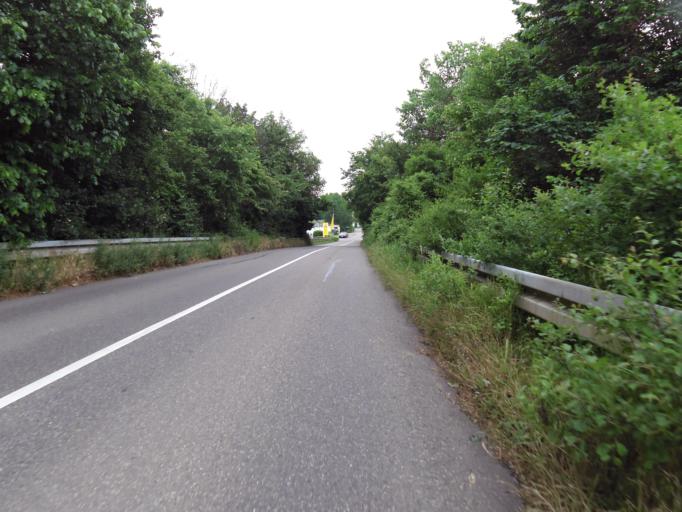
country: DE
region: Hesse
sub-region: Regierungsbezirk Darmstadt
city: Burstadt
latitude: 49.6415
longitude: 8.4476
